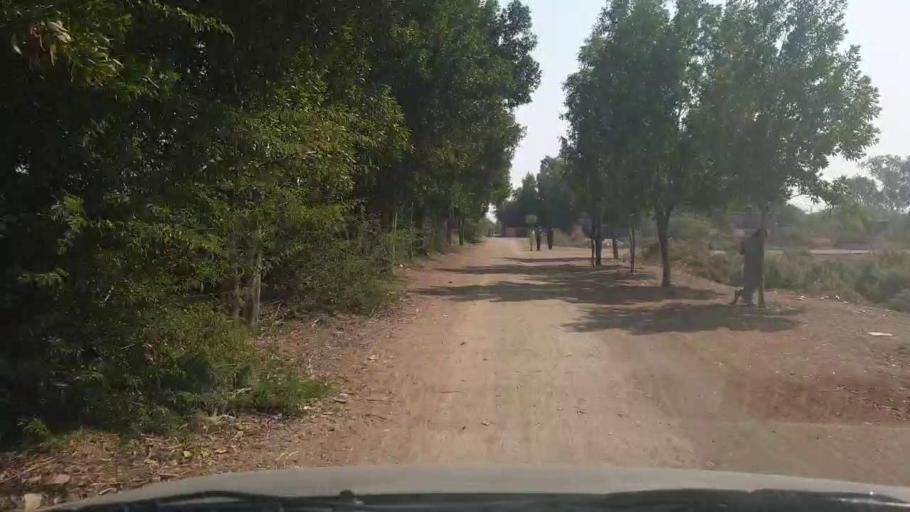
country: PK
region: Sindh
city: Mirwah Gorchani
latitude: 25.2761
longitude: 69.1360
